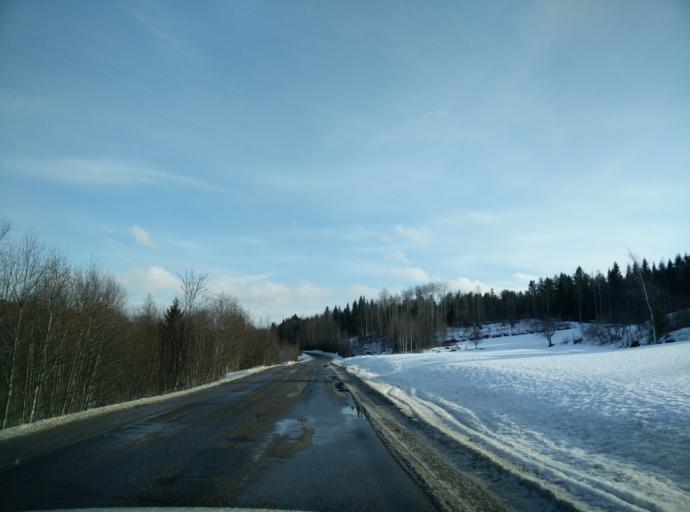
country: SE
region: Vaesternorrland
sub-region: Sundsvalls Kommun
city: Njurundabommen
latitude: 62.2212
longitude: 17.3389
